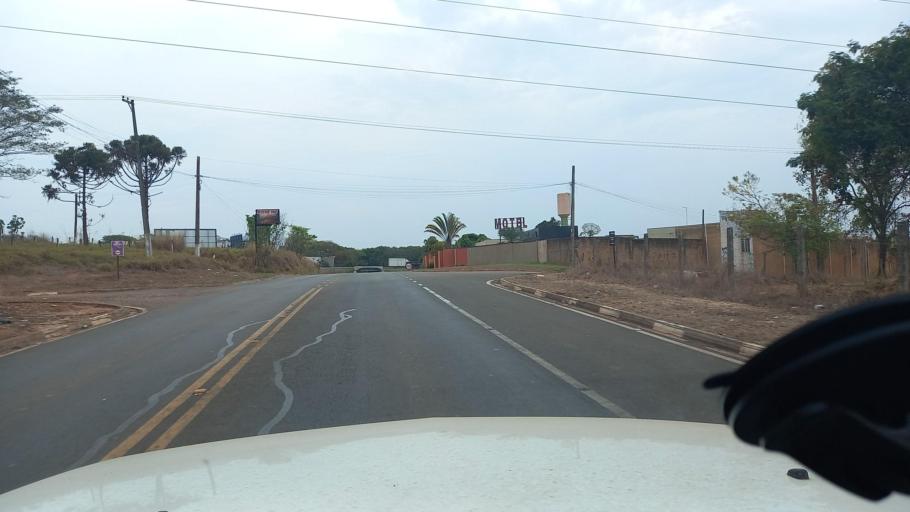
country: BR
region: Sao Paulo
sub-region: Moji-Guacu
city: Mogi-Gaucu
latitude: -22.3740
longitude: -46.9685
